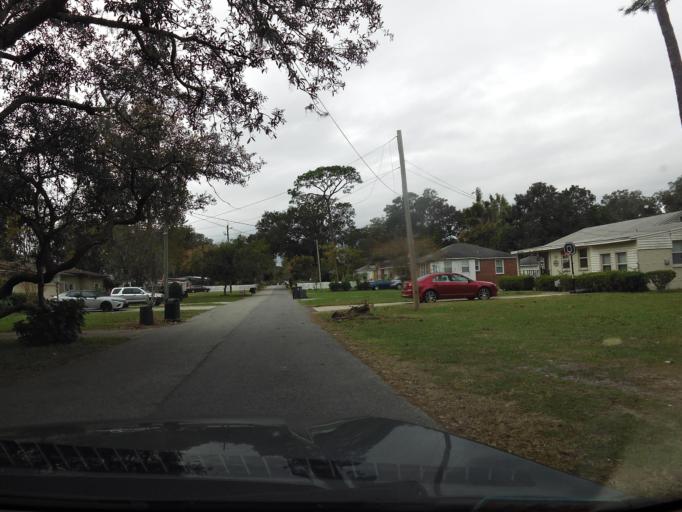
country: US
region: Florida
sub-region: Duval County
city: Jacksonville
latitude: 30.3058
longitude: -81.6034
